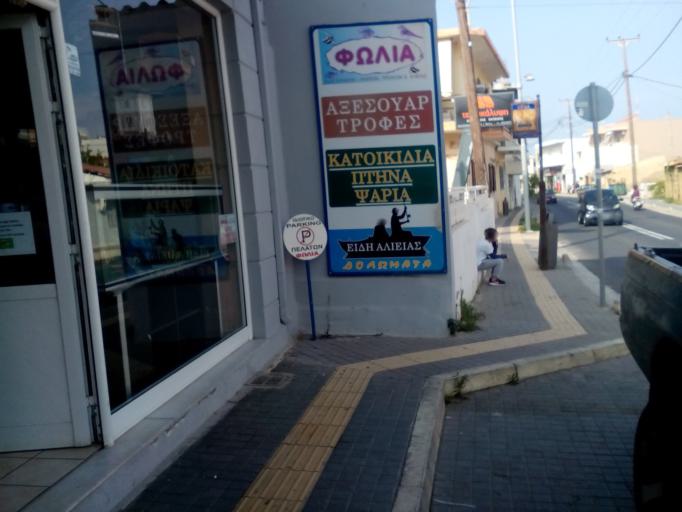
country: GR
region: Crete
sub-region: Nomos Rethymnis
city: Rethymno
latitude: 35.3664
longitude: 24.5060
